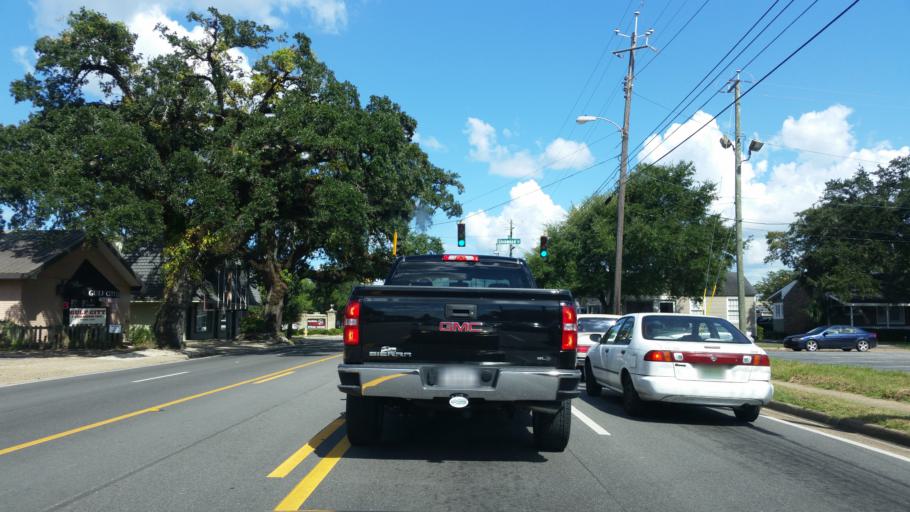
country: US
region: Alabama
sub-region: Mobile County
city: Mobile
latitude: 30.6764
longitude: -88.0913
